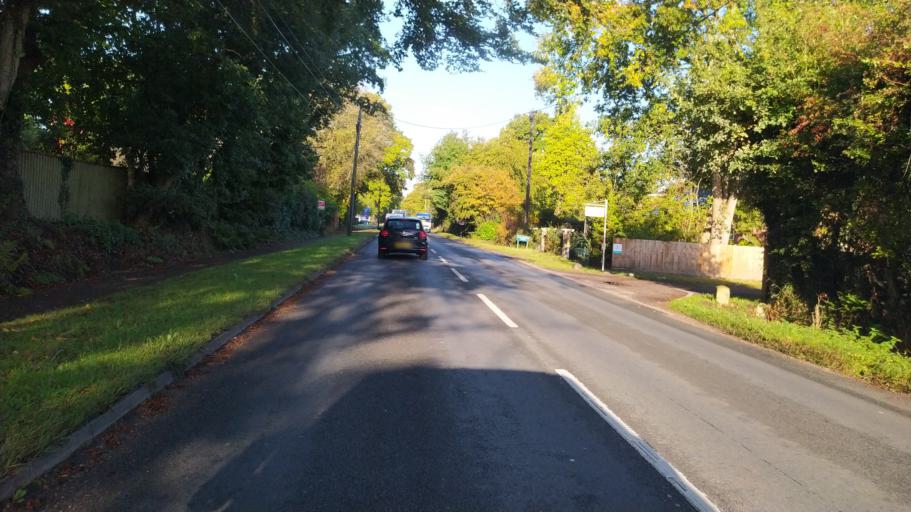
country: GB
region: England
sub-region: Dorset
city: Three Legged Cross
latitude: 50.8478
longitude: -1.8762
